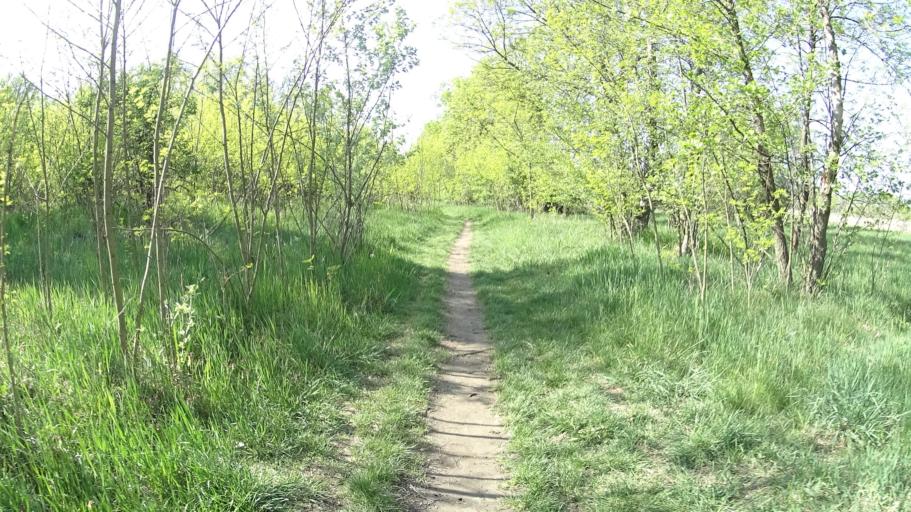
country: HU
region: Pest
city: Vecses
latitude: 47.4461
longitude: 19.2806
